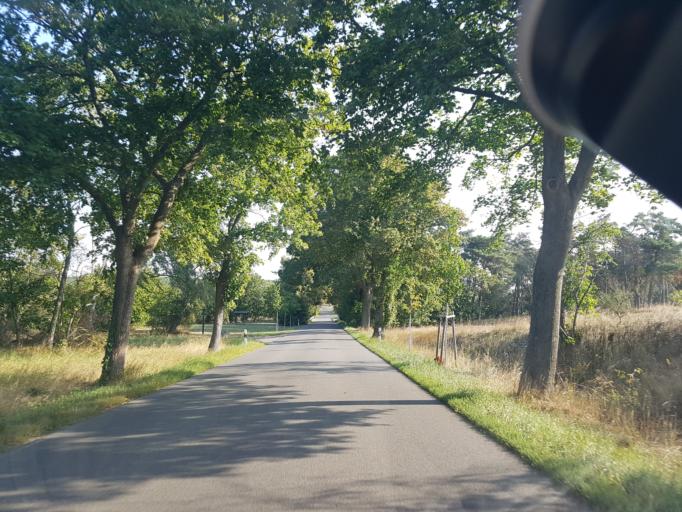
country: DE
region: Brandenburg
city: Niemegk
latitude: 52.0008
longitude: 12.6808
